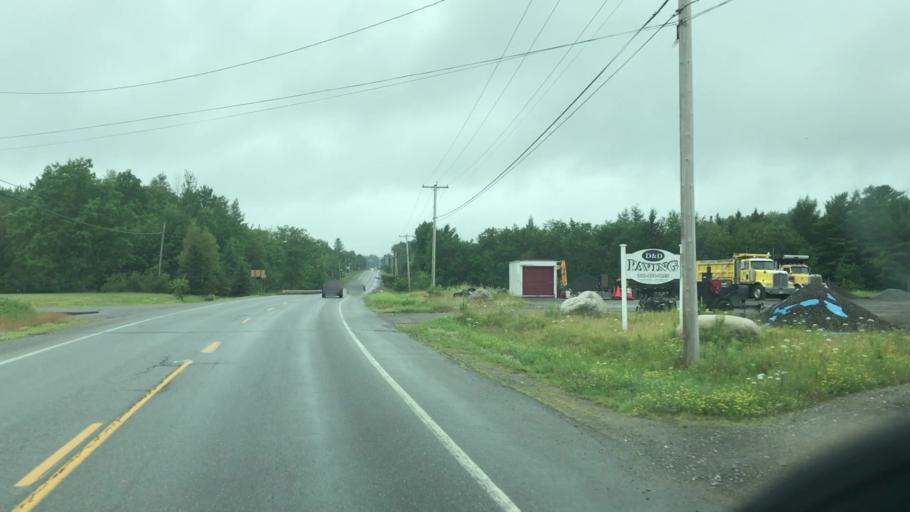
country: US
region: Maine
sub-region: Penobscot County
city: Lincoln
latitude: 45.3528
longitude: -68.5343
